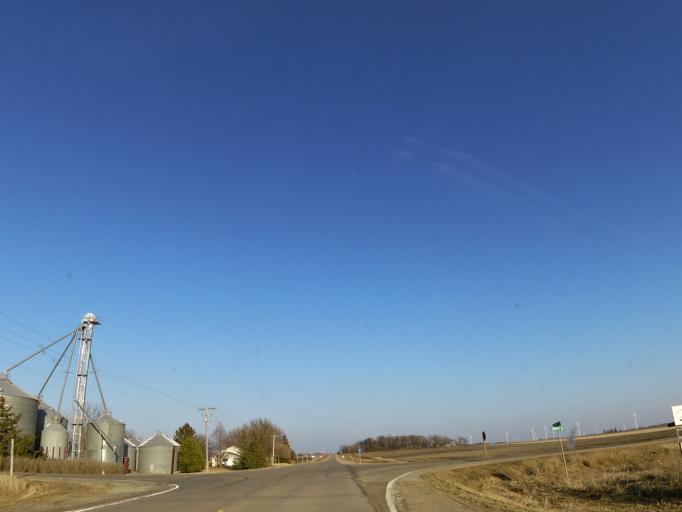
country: US
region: Iowa
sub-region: Worth County
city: Northwood
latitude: 43.4404
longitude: -93.1249
